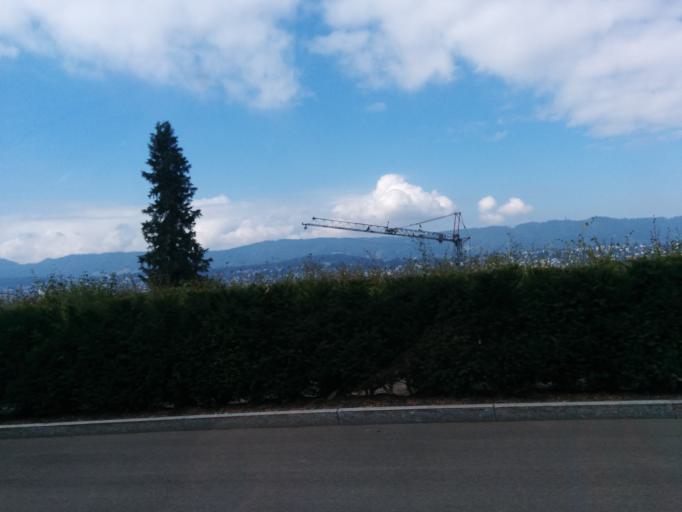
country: CH
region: Zurich
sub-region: Bezirk Meilen
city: Kuesnacht / Goldbach
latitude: 47.3282
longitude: 8.5807
